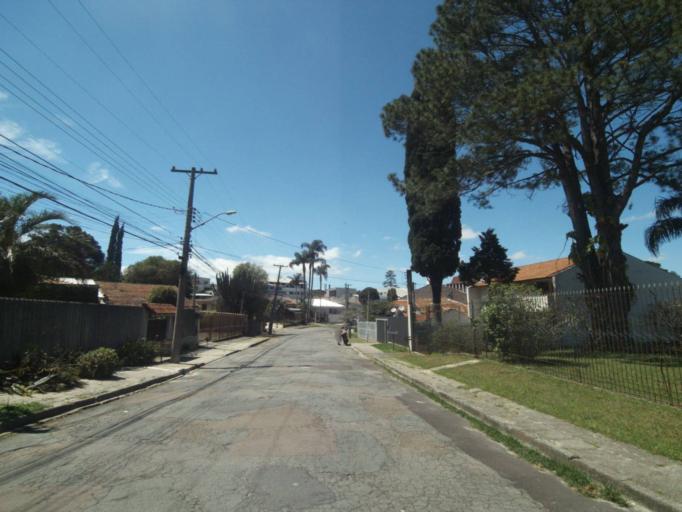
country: BR
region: Parana
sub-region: Curitiba
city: Curitiba
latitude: -25.3888
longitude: -49.2622
